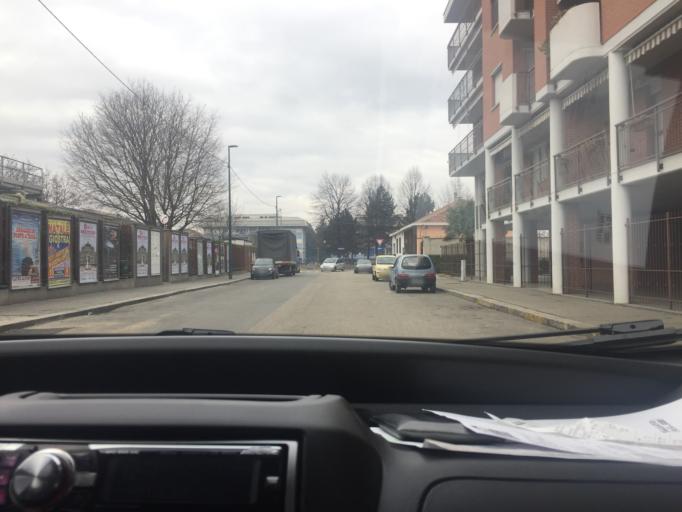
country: IT
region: Piedmont
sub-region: Provincia di Torino
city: Lesna
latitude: 45.0816
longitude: 7.6170
